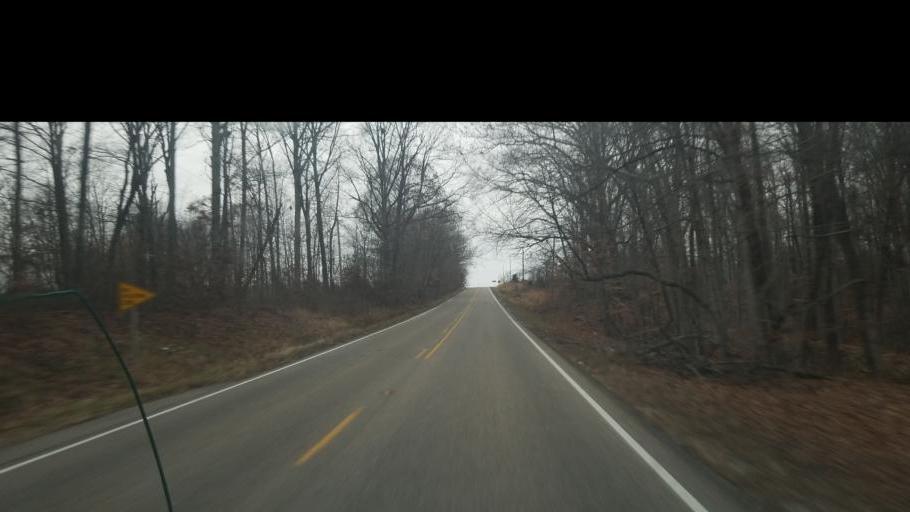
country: US
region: Indiana
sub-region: Clay County
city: Middlebury
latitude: 39.3653
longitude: -86.9655
